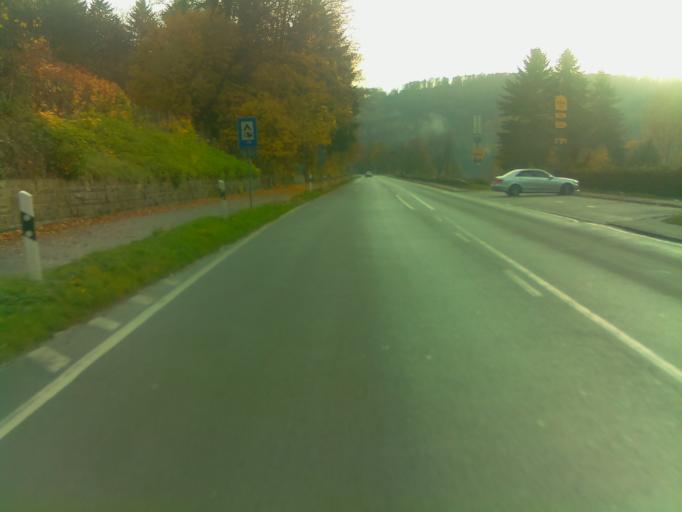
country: DE
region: Baden-Wuerttemberg
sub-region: Karlsruhe Region
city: Neckargemund
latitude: 49.4030
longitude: 8.7804
